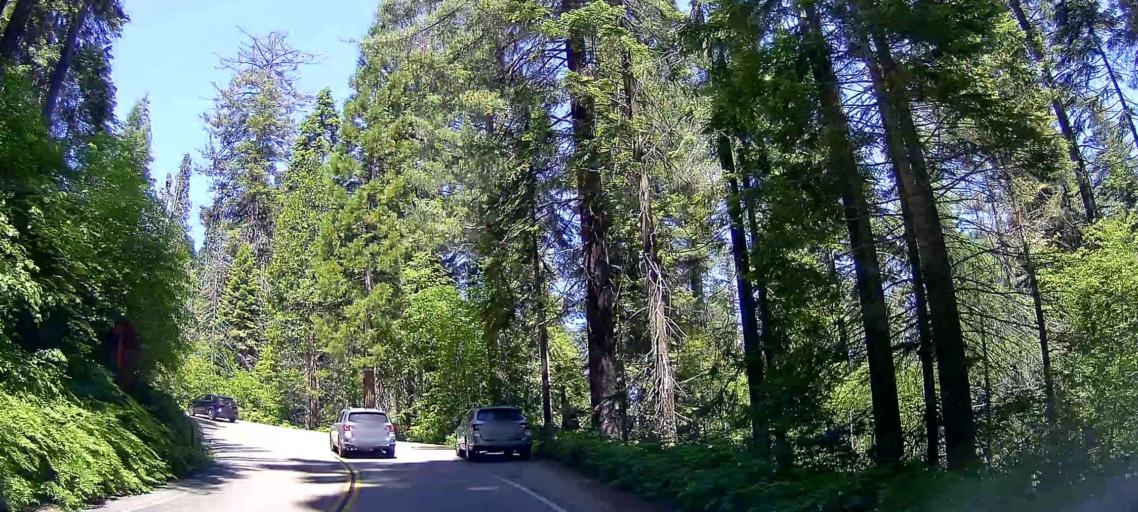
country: US
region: California
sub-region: Tulare County
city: Three Rivers
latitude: 36.5553
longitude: -118.7799
